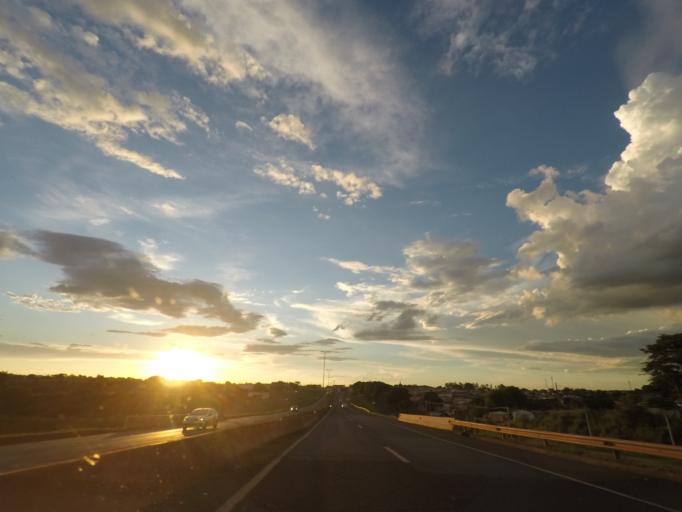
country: BR
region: Minas Gerais
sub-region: Uberaba
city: Uberaba
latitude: -19.7793
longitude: -47.9608
